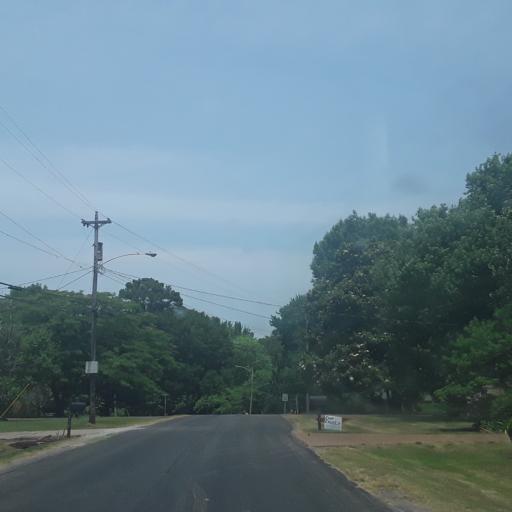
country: US
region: Tennessee
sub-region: Williamson County
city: Brentwood
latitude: 36.0573
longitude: -86.7555
